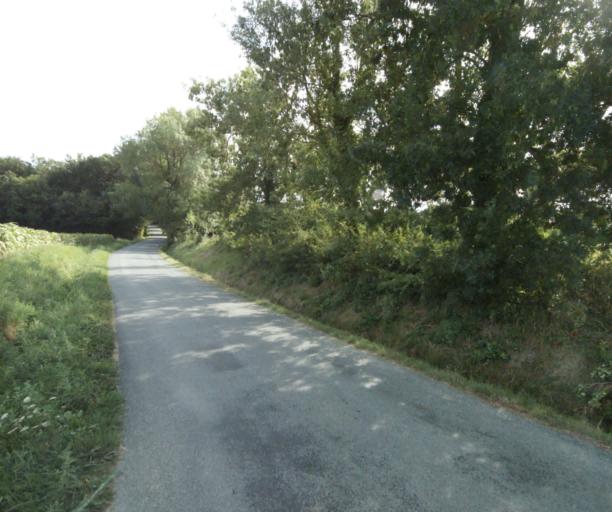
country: FR
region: Midi-Pyrenees
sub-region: Departement du Tarn
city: Puylaurens
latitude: 43.5478
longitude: 2.0602
